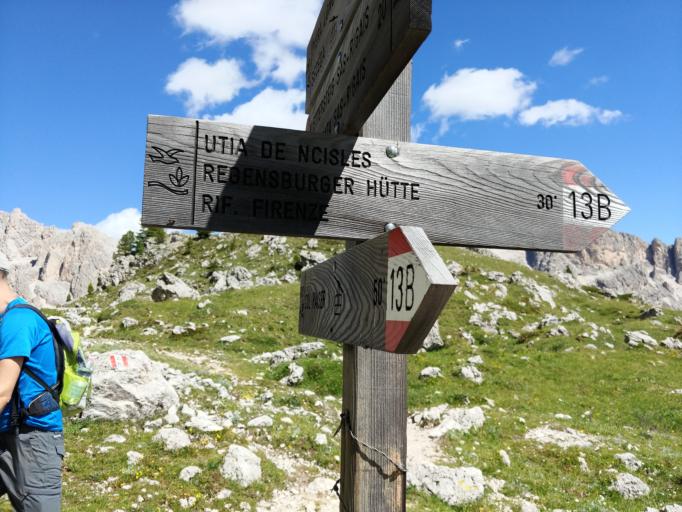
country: IT
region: Trentino-Alto Adige
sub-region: Bolzano
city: Santa Cristina Valgardena
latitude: 46.5988
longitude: 11.7568
